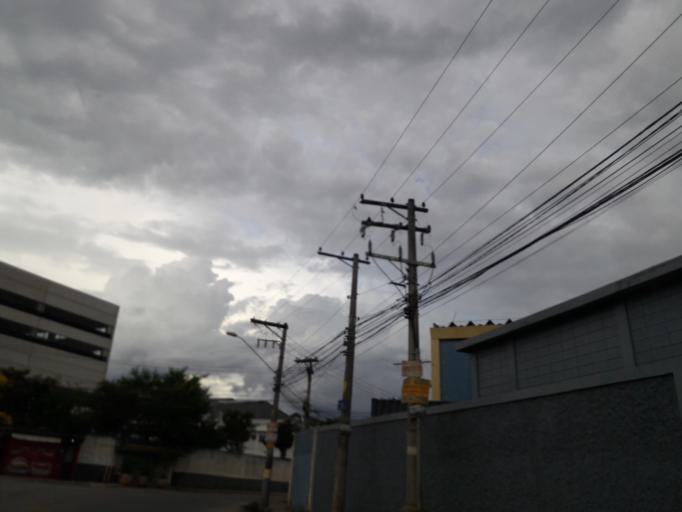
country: BR
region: Sao Paulo
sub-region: Aruja
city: Aruja
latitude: -23.4179
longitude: -46.3948
